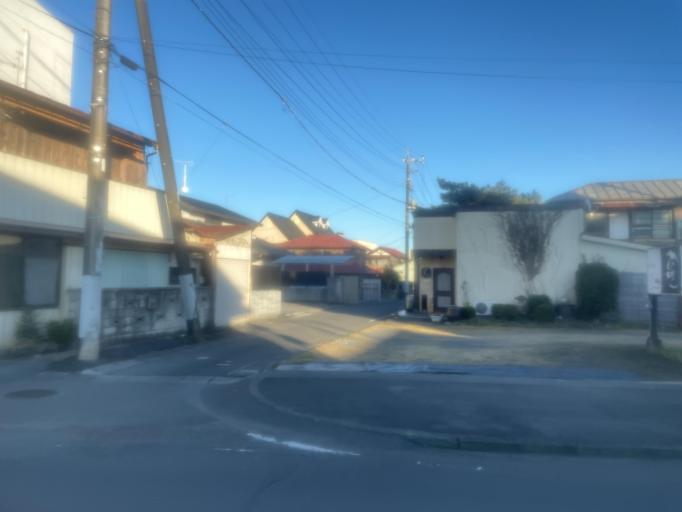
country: JP
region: Saitama
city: Yorii
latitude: 36.1138
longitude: 139.1956
